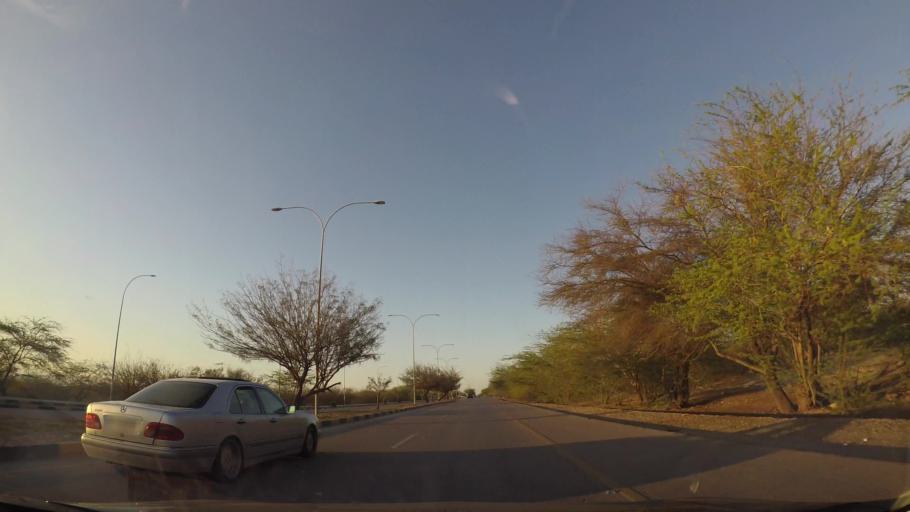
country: PS
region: West Bank
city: Jericho
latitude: 31.7673
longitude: 35.5927
